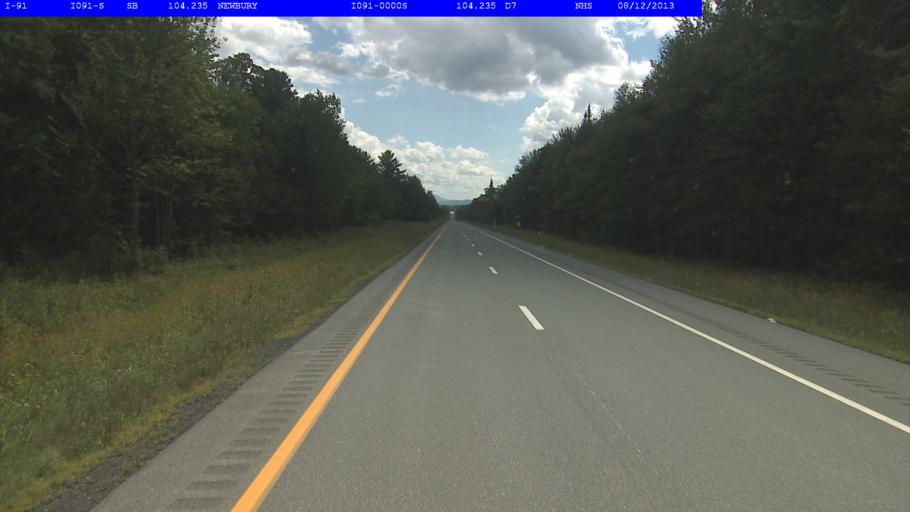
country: US
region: New Hampshire
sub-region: Grafton County
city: Haverhill
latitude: 44.0747
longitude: -72.1126
